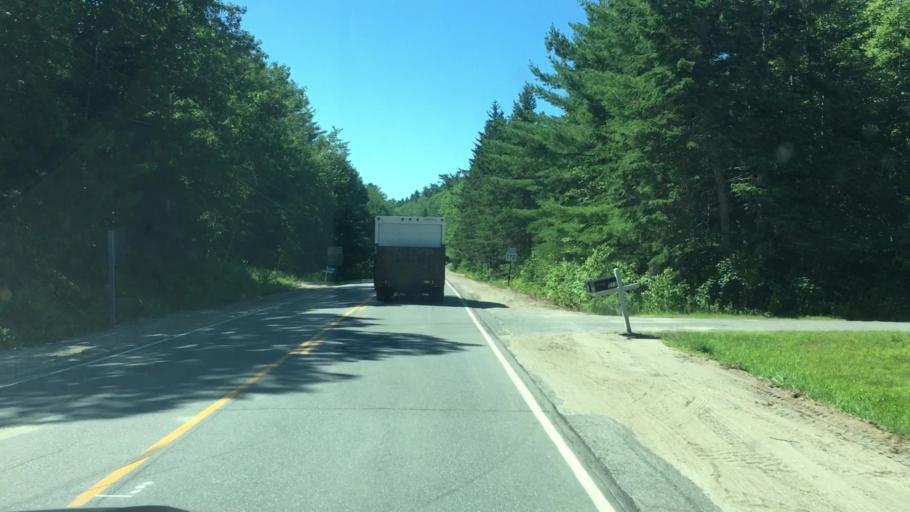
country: US
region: Maine
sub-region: Hancock County
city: Sedgwick
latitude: 44.3798
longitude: -68.5685
